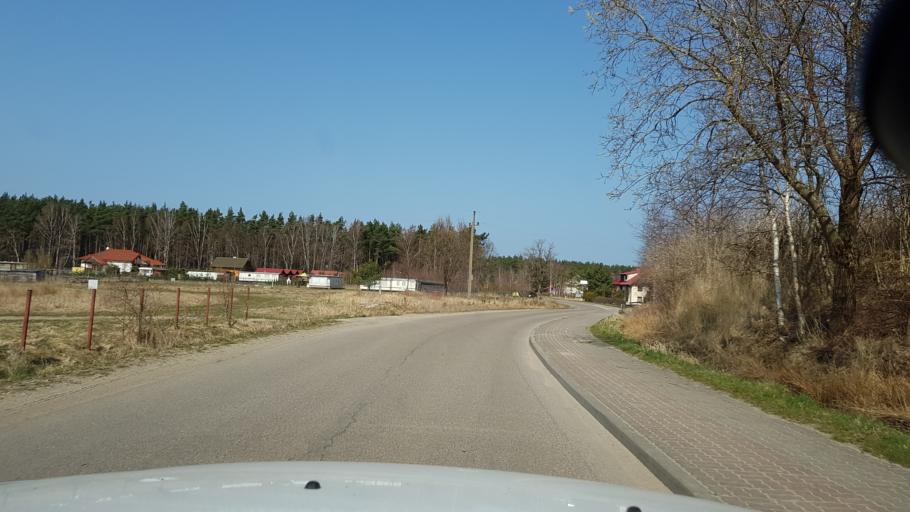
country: PL
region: West Pomeranian Voivodeship
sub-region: Powiat slawienski
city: Darlowo
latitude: 54.5178
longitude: 16.5141
